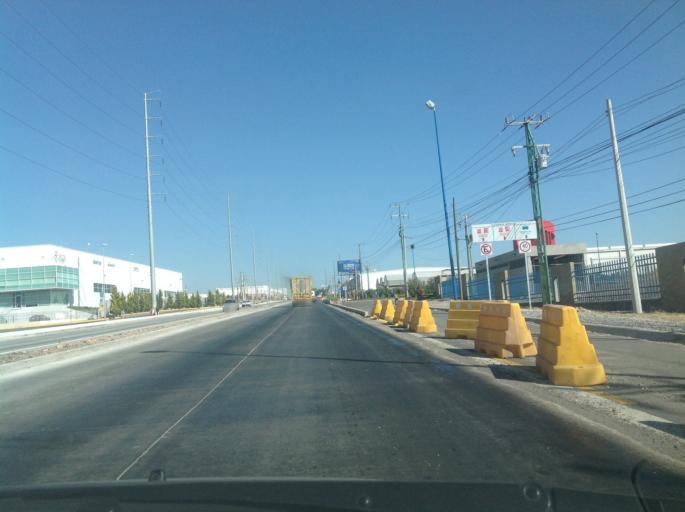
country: MX
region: Queretaro
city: El Colorado
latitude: 20.5547
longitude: -100.2670
